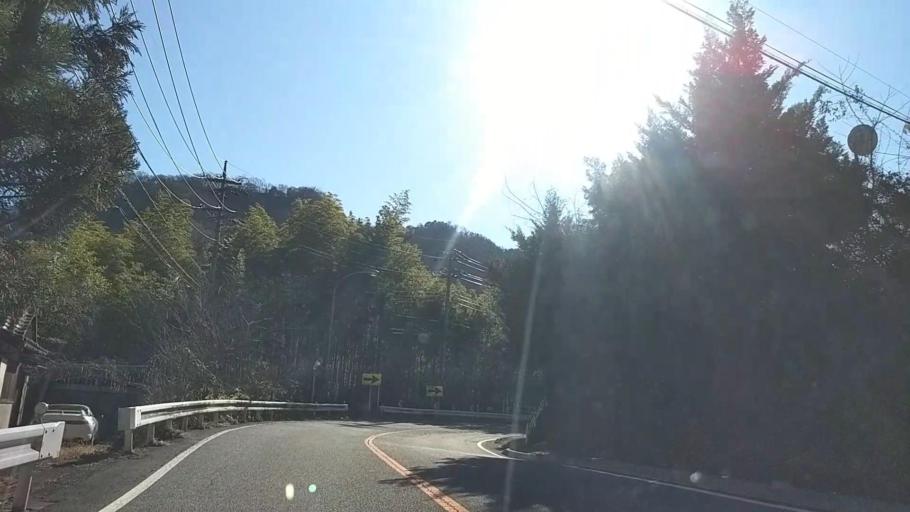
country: JP
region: Yamanashi
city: Uenohara
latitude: 35.6067
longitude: 139.0298
